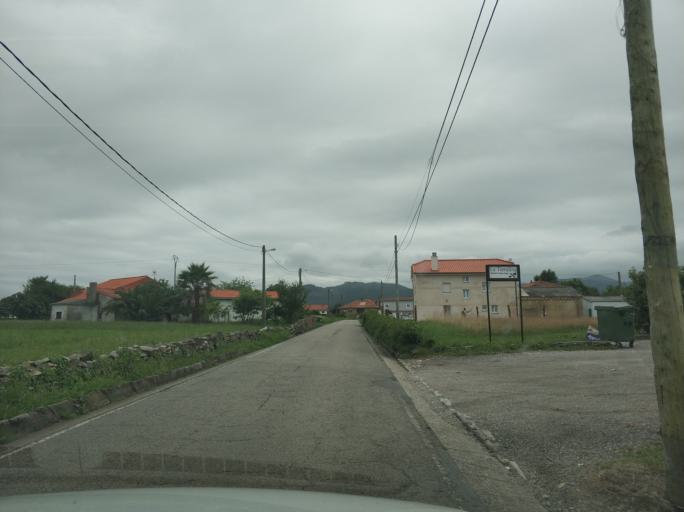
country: ES
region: Asturias
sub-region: Province of Asturias
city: Cudillero
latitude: 43.5732
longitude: -6.2383
